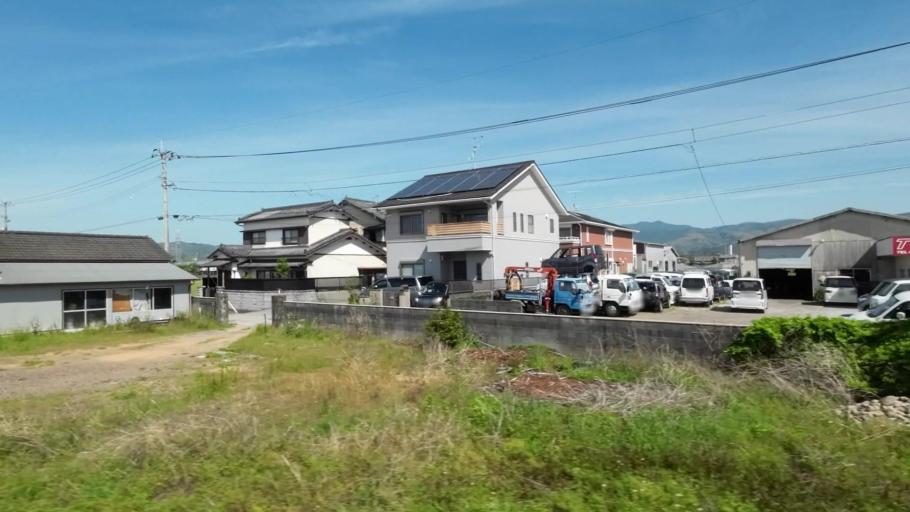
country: JP
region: Kochi
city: Kochi-shi
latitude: 33.5877
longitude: 133.6575
